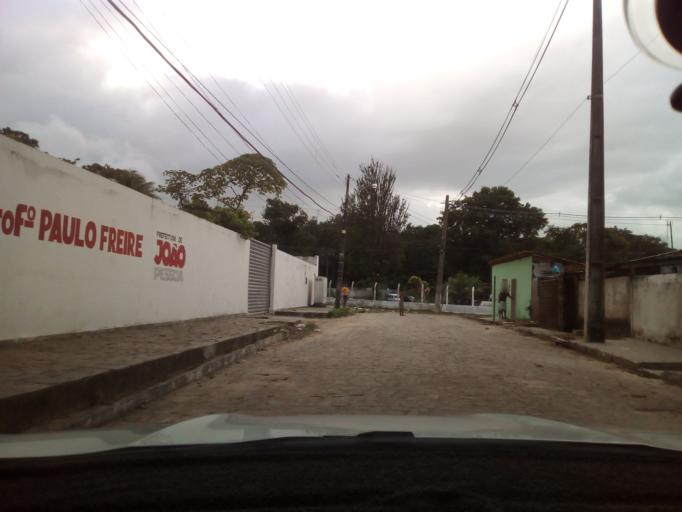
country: BR
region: Paraiba
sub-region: Bayeux
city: Bayeux
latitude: -7.1599
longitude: -34.9096
